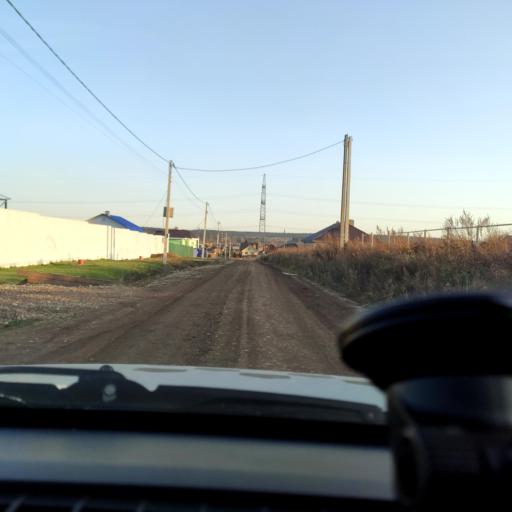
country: RU
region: Perm
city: Ferma
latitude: 57.9464
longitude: 56.3485
